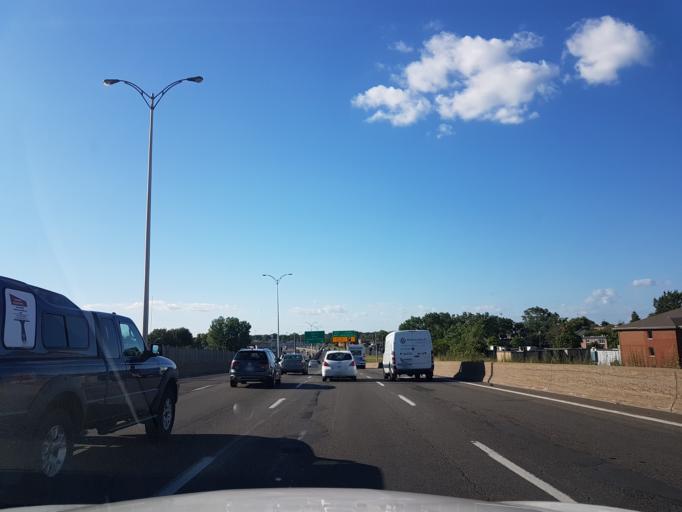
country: CA
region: Quebec
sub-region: Monteregie
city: Longueuil
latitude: 45.5052
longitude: -73.4892
